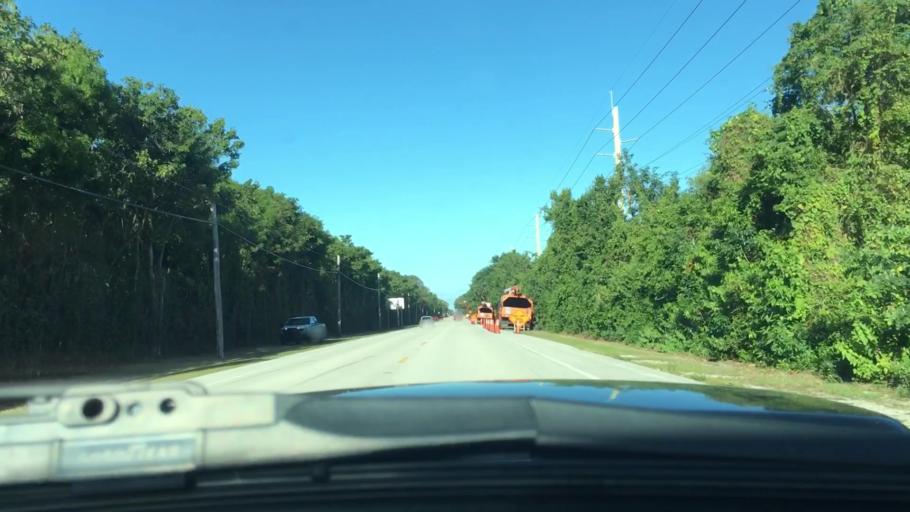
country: US
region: Florida
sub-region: Monroe County
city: North Key Largo
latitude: 25.1870
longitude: -80.3602
